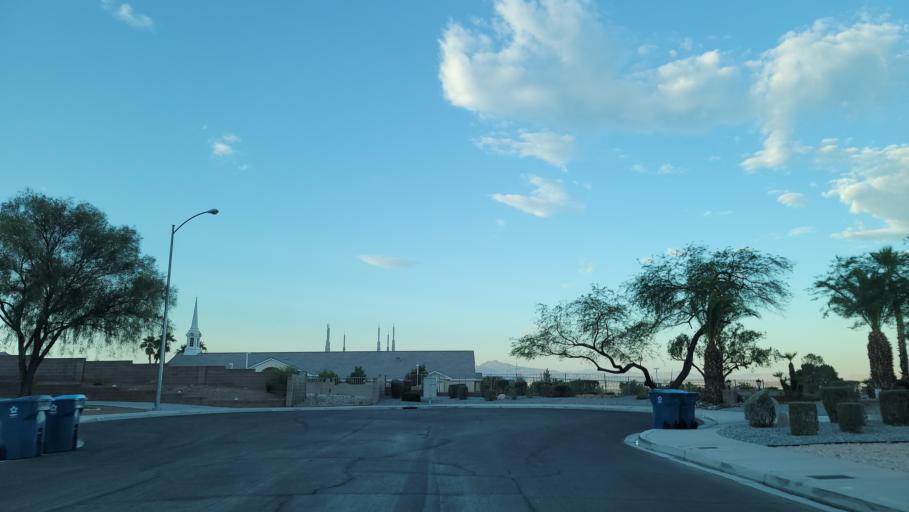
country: US
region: Nevada
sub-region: Clark County
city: Sunrise Manor
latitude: 36.1781
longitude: -115.0205
